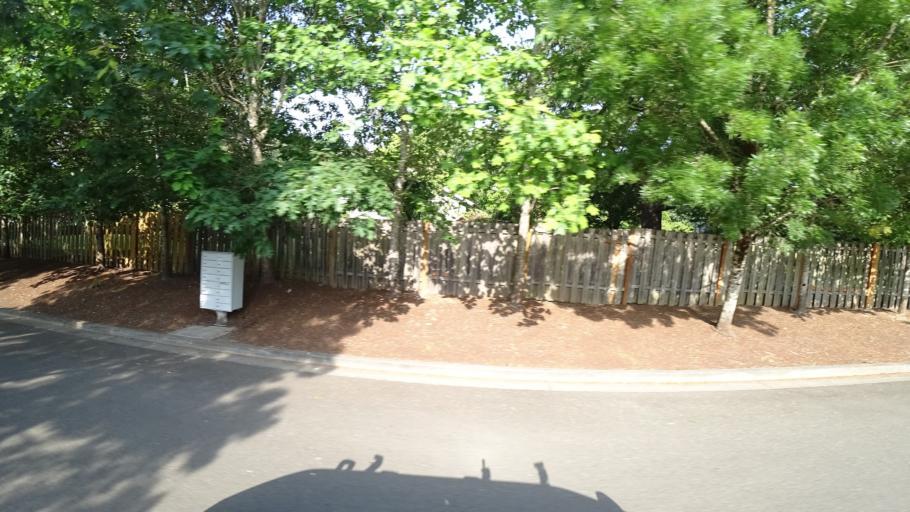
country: US
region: Oregon
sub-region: Clackamas County
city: Happy Valley
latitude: 45.4458
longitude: -122.5275
